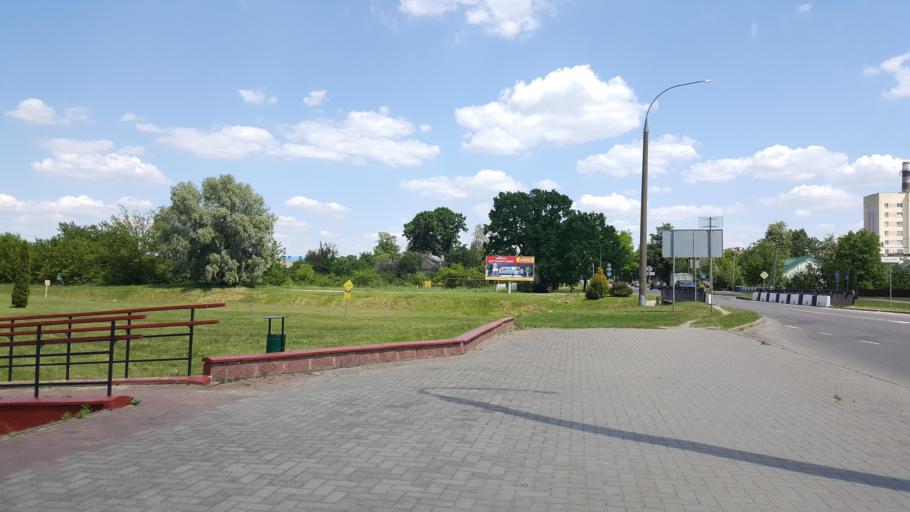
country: BY
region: Brest
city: Kobryn
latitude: 52.2092
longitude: 24.3319
